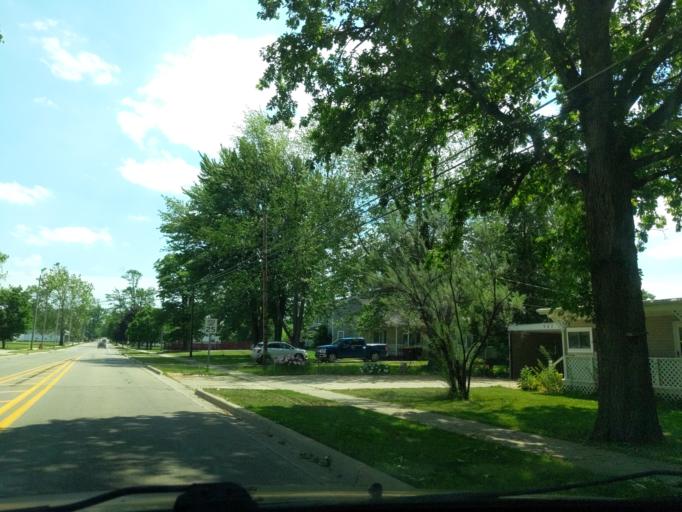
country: US
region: Michigan
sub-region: Clinton County
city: Saint Johns
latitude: 43.0117
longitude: -84.5627
